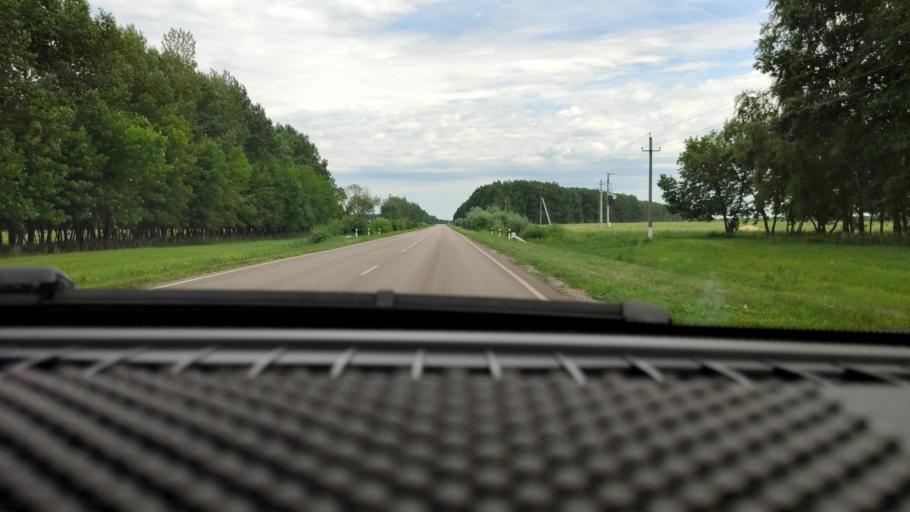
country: RU
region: Voronezj
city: Panino
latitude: 51.6623
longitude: 39.9815
